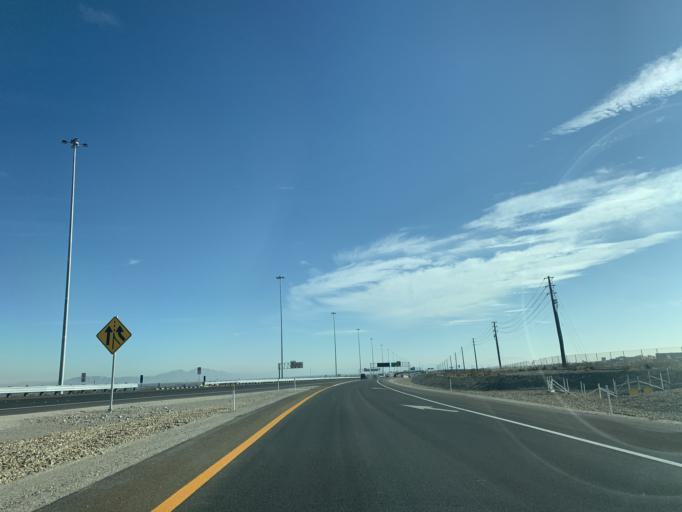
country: US
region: Nevada
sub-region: Clark County
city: Summerlin South
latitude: 36.3240
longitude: -115.3098
